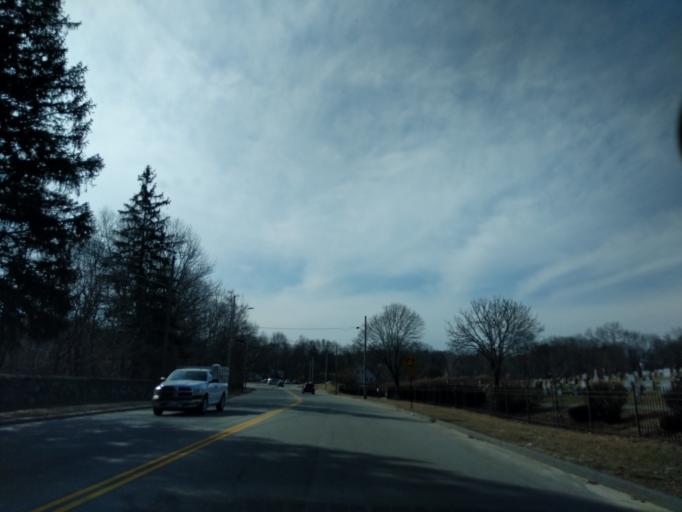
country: US
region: Massachusetts
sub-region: Worcester County
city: Auburn
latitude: 42.2339
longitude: -71.8337
